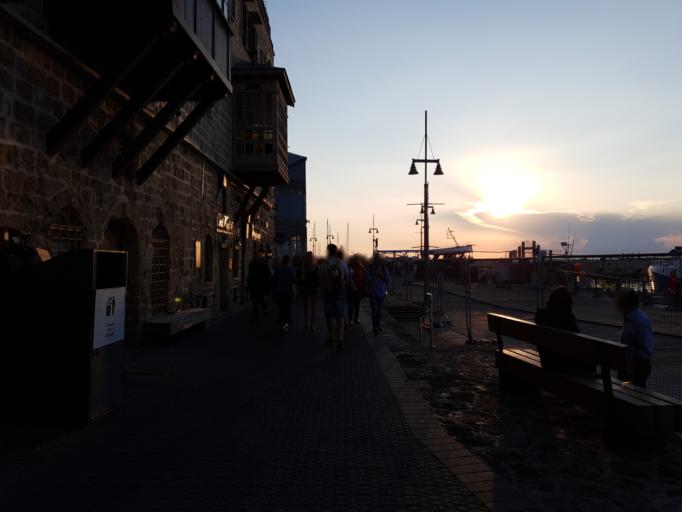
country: IL
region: Tel Aviv
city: Yafo
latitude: 32.0540
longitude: 34.7506
